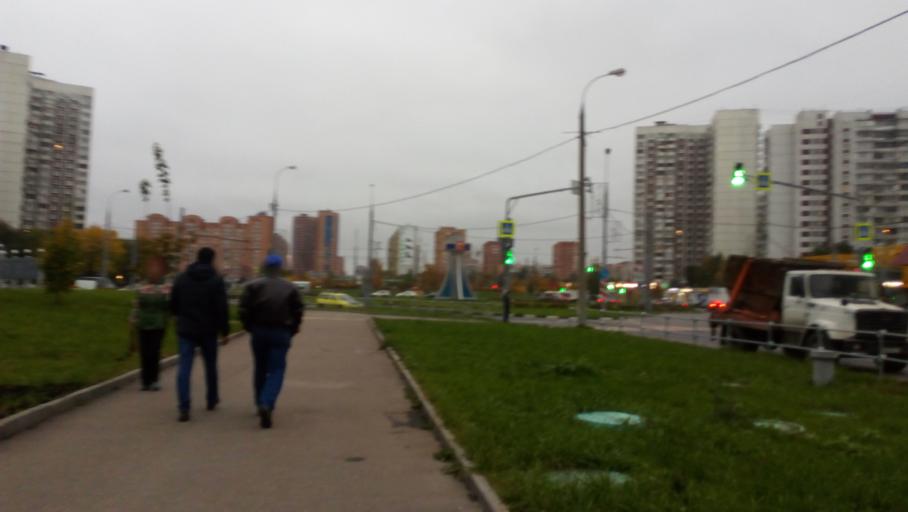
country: RU
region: Moskovskaya
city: Reutov
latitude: 55.7414
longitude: 37.8660
